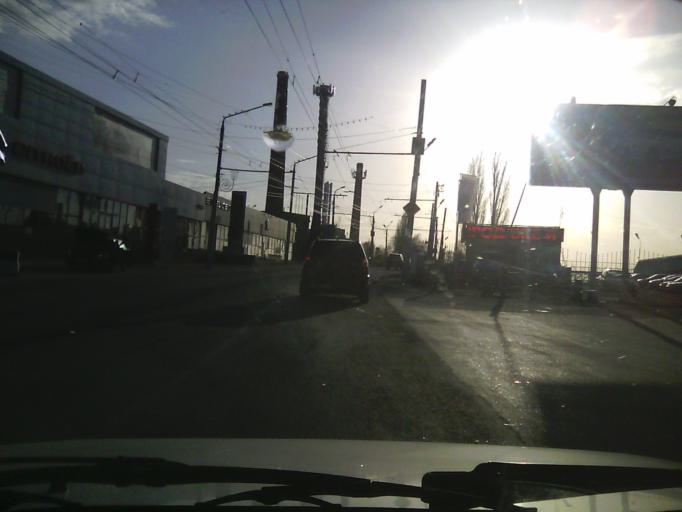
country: RU
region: Saratov
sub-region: Saratovskiy Rayon
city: Saratov
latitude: 51.5917
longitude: 45.9395
